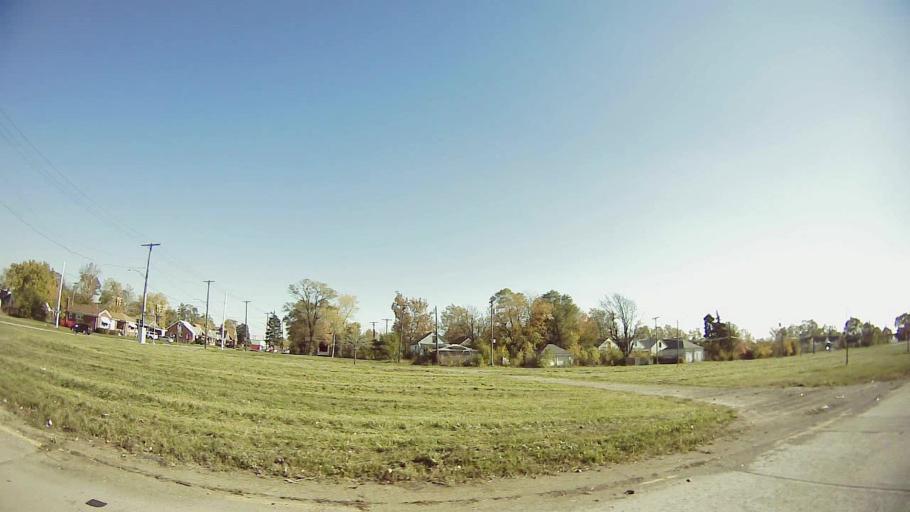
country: US
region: Michigan
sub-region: Wayne County
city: Hamtramck
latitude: 42.4117
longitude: -83.0431
